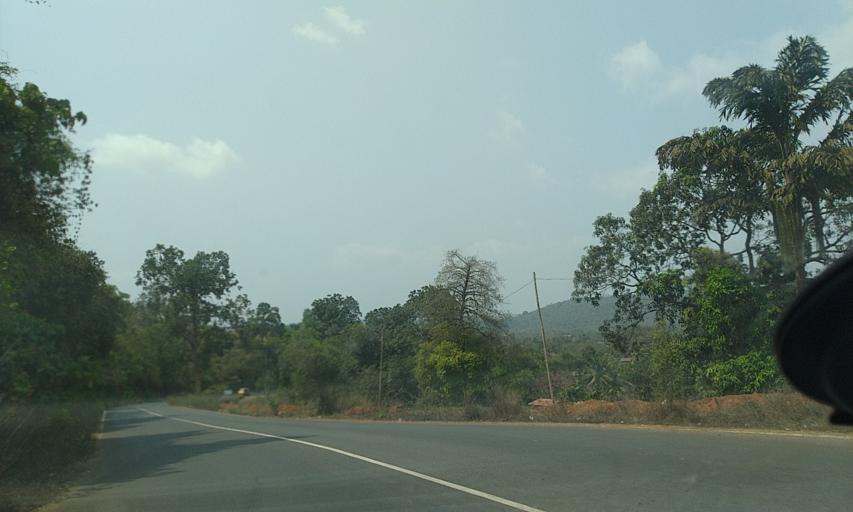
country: IN
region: Goa
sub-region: North Goa
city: Pernem
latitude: 15.7102
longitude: 73.7990
